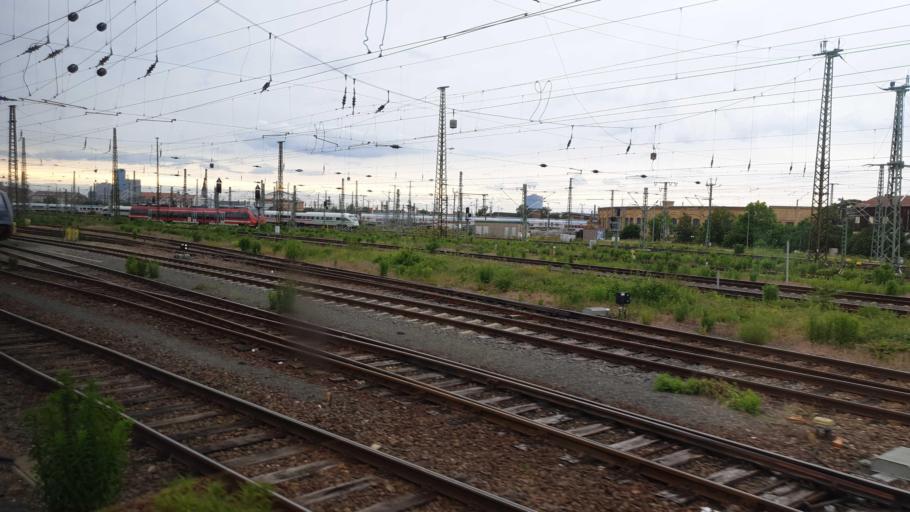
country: DE
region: Saxony
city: Leipzig
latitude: 51.3504
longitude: 12.3922
